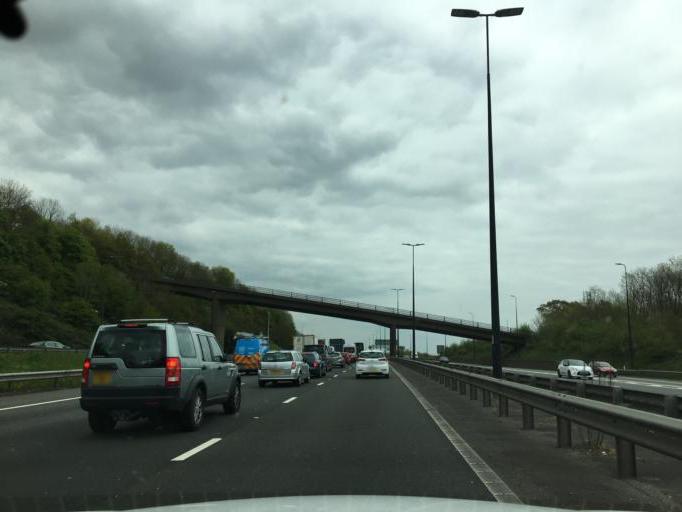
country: GB
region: Wales
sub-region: Newport
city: Marshfield
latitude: 51.5517
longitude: -3.0671
